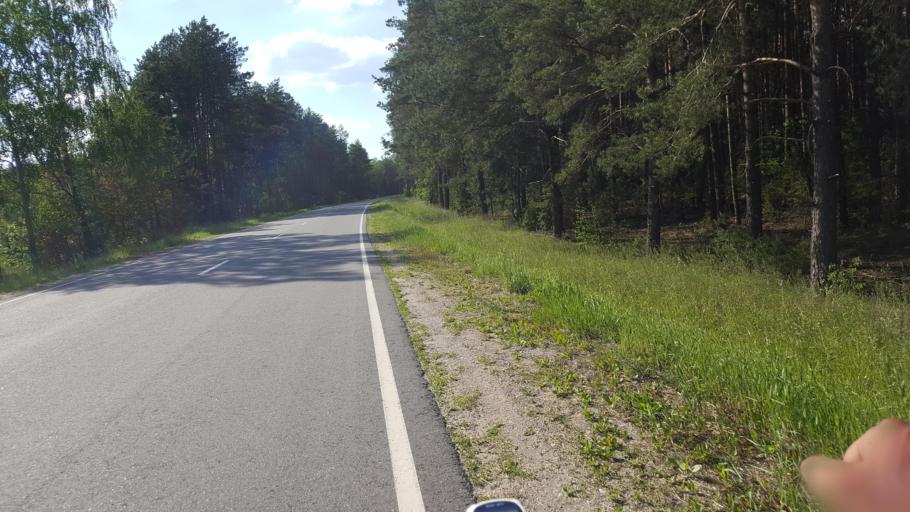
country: BY
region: Brest
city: Zhabinka
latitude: 52.3754
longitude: 24.1306
